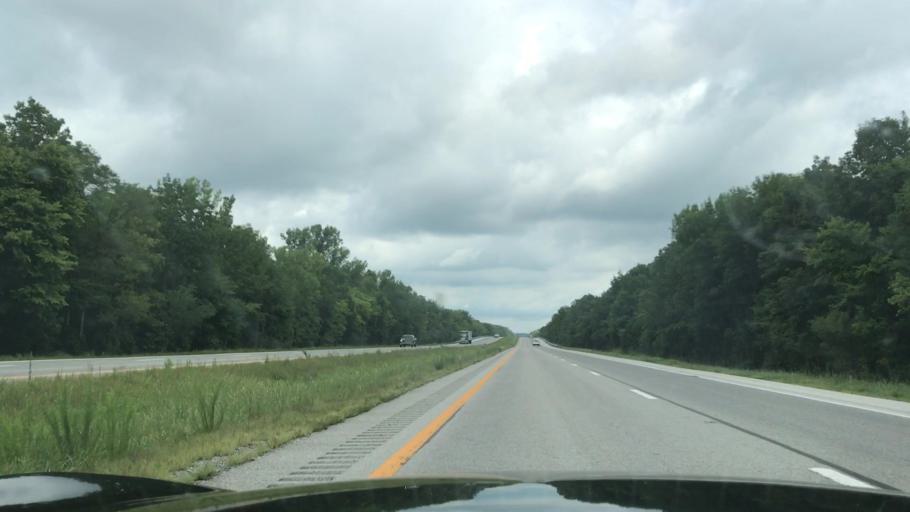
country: US
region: Kentucky
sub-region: Butler County
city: Morgantown
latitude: 37.1305
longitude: -86.6467
